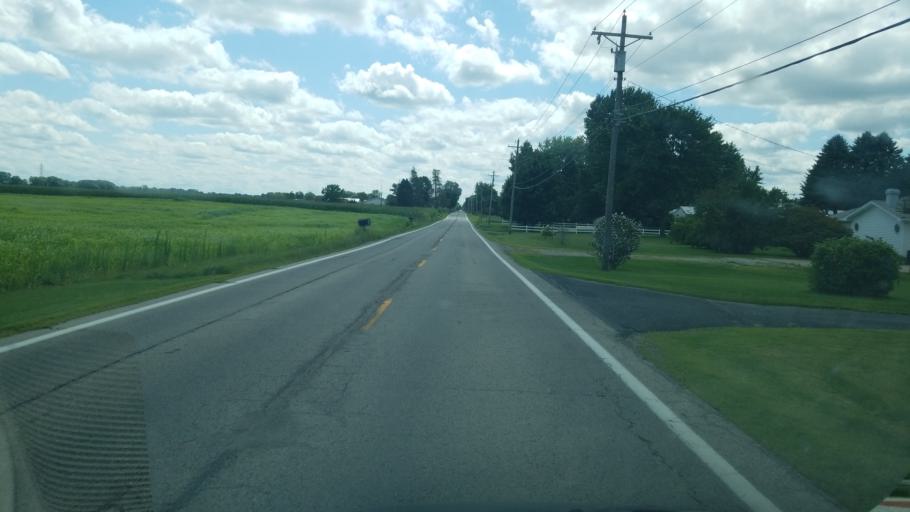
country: US
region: Ohio
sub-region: Henry County
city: Liberty Center
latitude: 41.4808
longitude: -84.0088
